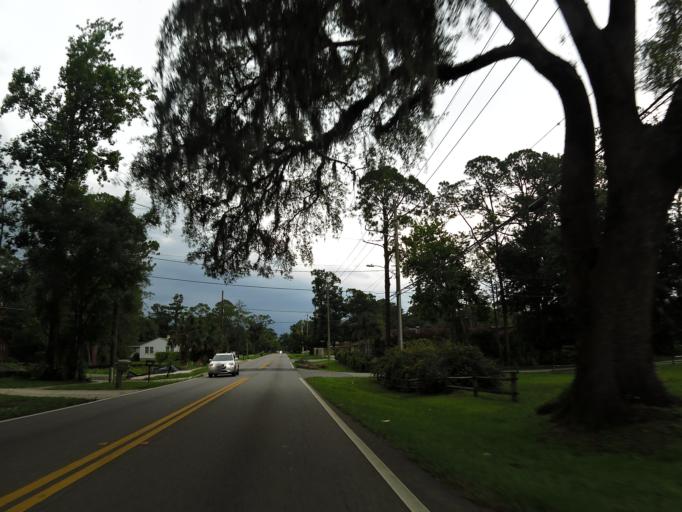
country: US
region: Florida
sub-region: Duval County
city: Jacksonville
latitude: 30.2756
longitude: -81.5895
